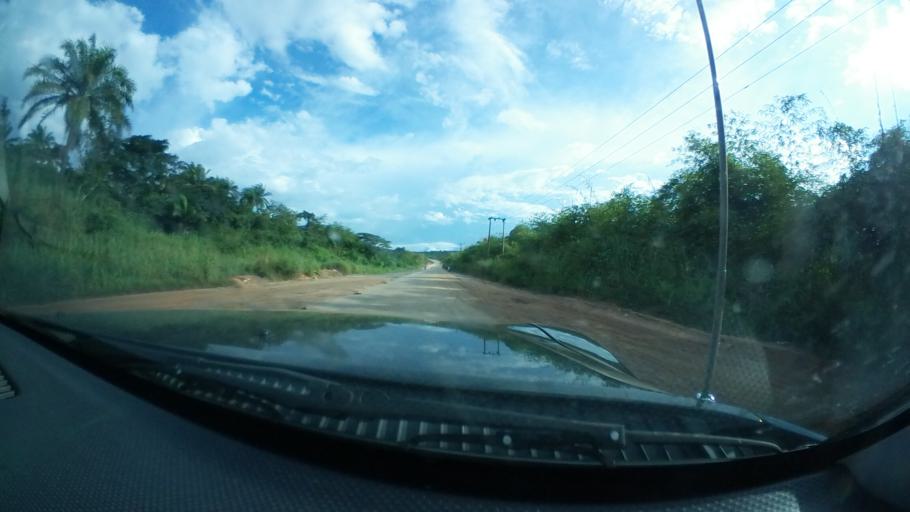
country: NG
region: Imo
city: Orodo
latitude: 5.6940
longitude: 7.0106
